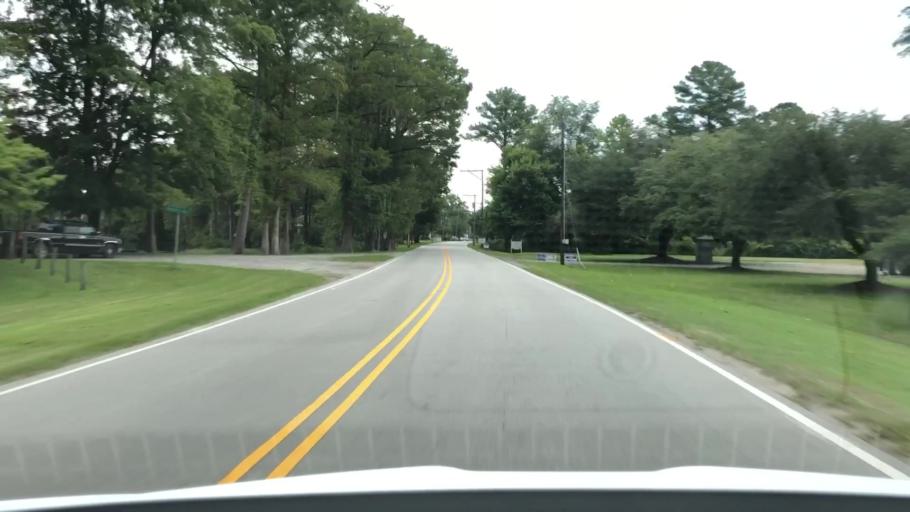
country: US
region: North Carolina
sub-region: Jones County
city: Trenton
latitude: 35.0601
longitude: -77.3552
